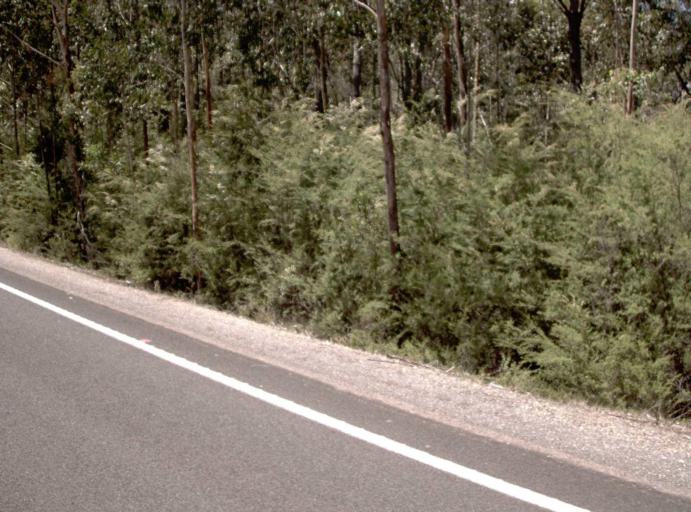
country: AU
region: Victoria
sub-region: East Gippsland
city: Lakes Entrance
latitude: -37.6943
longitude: 148.6132
